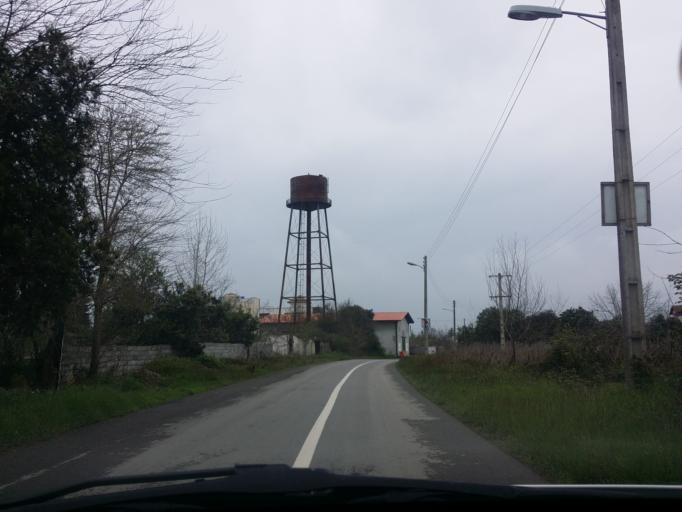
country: IR
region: Mazandaran
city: Chalus
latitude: 36.6843
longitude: 51.3797
